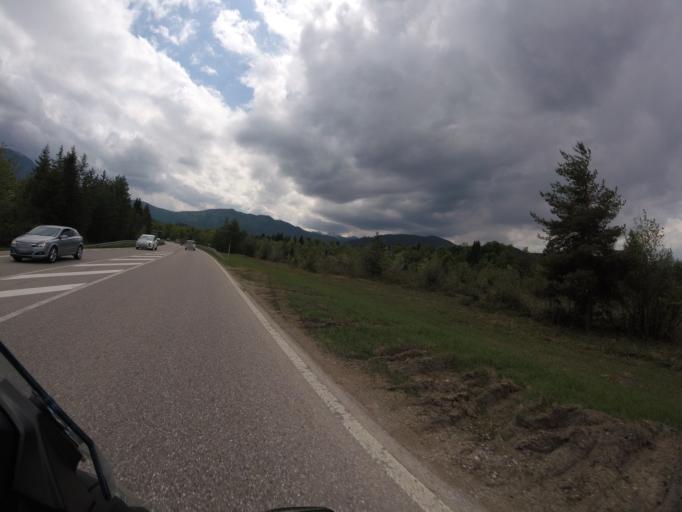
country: DE
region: Bavaria
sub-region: Upper Bavaria
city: Lenggries
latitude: 47.6602
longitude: 11.5851
